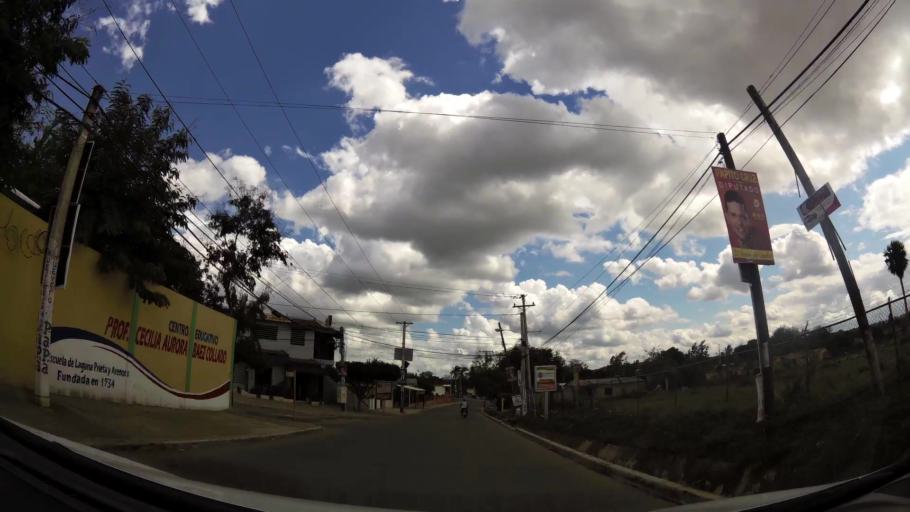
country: DO
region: Santiago
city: Licey al Medio
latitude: 19.3970
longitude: -70.6488
